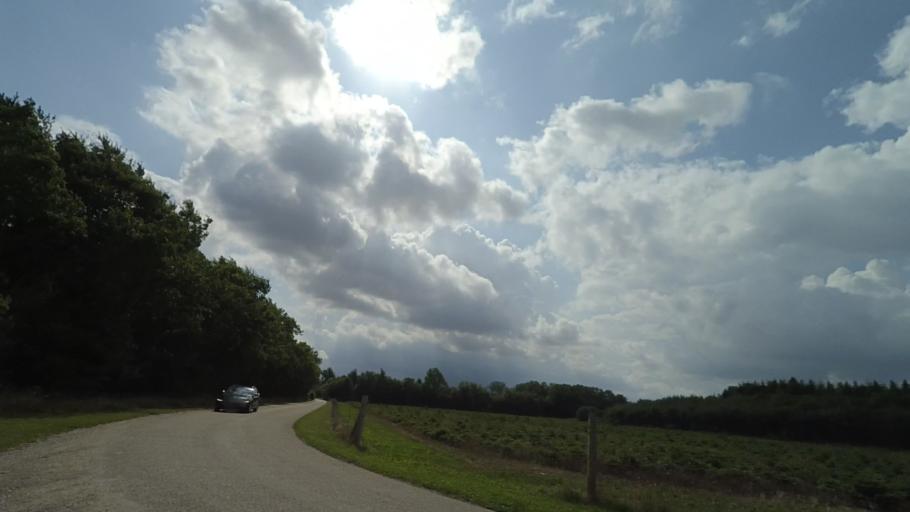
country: DK
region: Central Jutland
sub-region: Norddjurs Kommune
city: Allingabro
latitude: 56.5469
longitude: 10.3655
